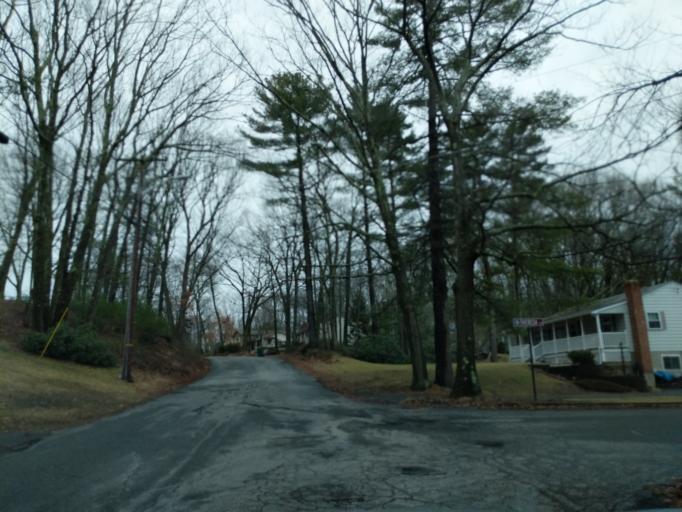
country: US
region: Massachusetts
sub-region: Worcester County
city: Whitinsville
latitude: 42.1075
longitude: -71.6931
